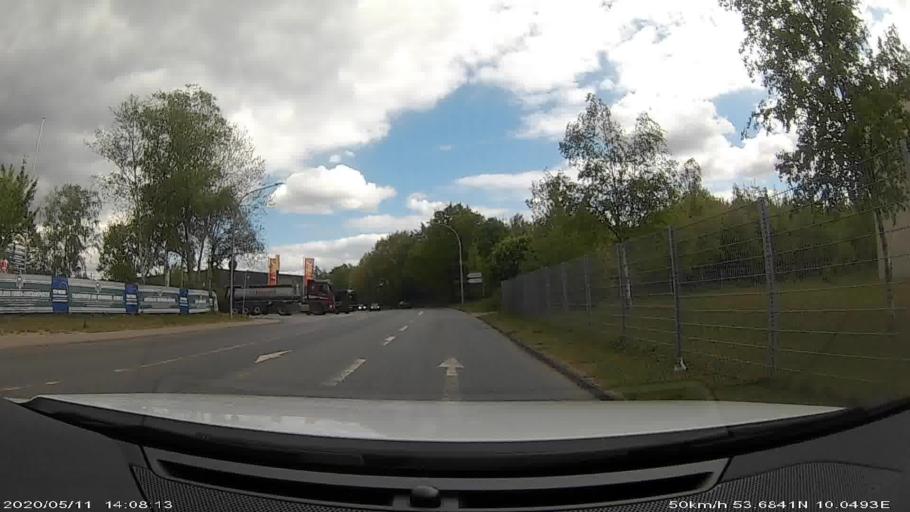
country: DE
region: Hamburg
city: Lemsahl-Mellingstedt
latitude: 53.6833
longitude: 10.0709
